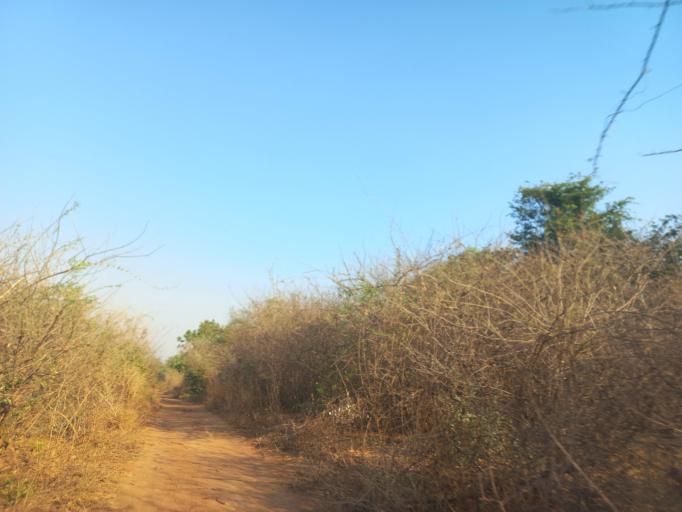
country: ZM
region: Lusaka
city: Luangwa
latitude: -15.4207
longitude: 30.2626
